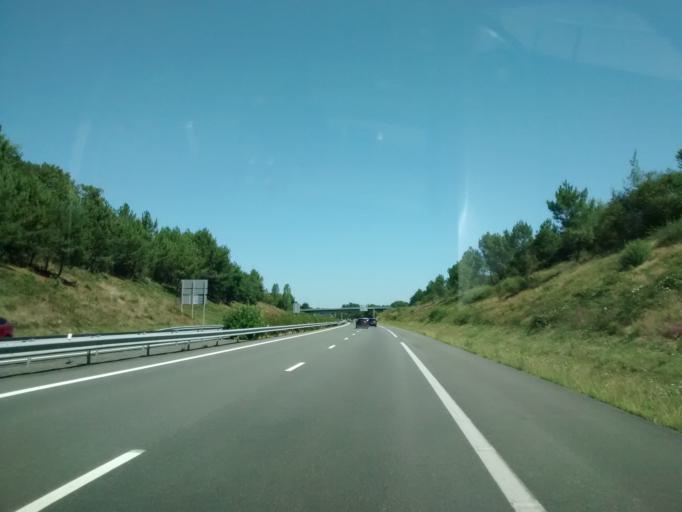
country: FR
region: Aquitaine
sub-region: Departement de la Dordogne
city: Montpon-Menesterol
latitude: 44.9821
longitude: 0.1454
